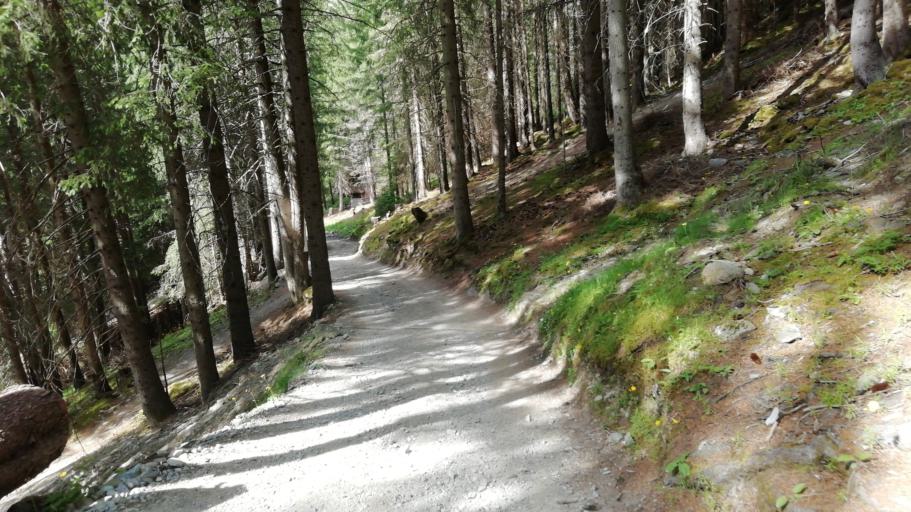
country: IT
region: Lombardy
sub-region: Provincia di Sondrio
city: Sant'Antonio
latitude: 46.4725
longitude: 10.4485
